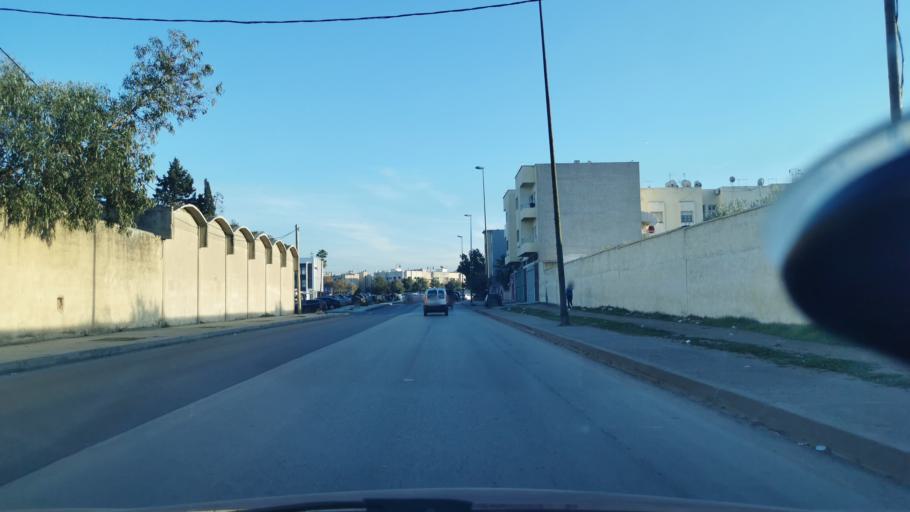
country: MA
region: Fes-Boulemane
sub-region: Fes
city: Fes
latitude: 34.0225
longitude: -4.9833
